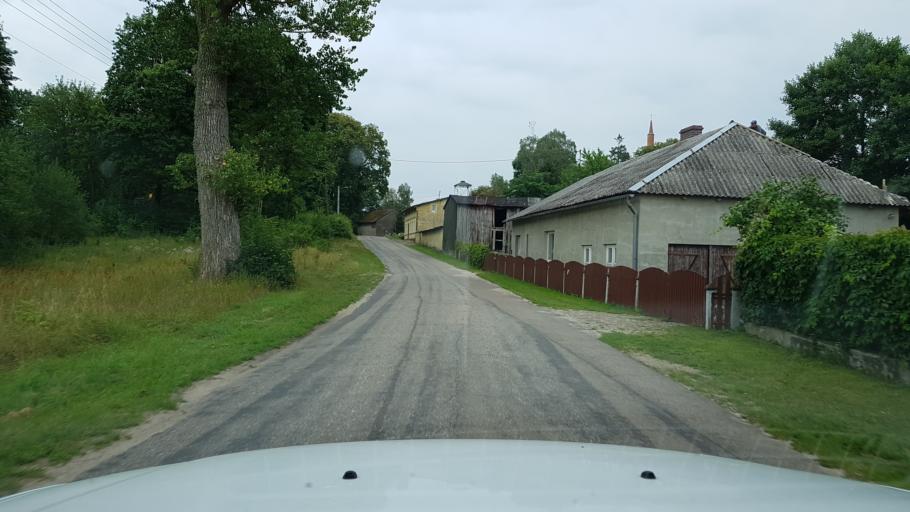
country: PL
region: West Pomeranian Voivodeship
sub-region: Powiat koszalinski
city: Bobolice
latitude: 53.9293
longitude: 16.6547
